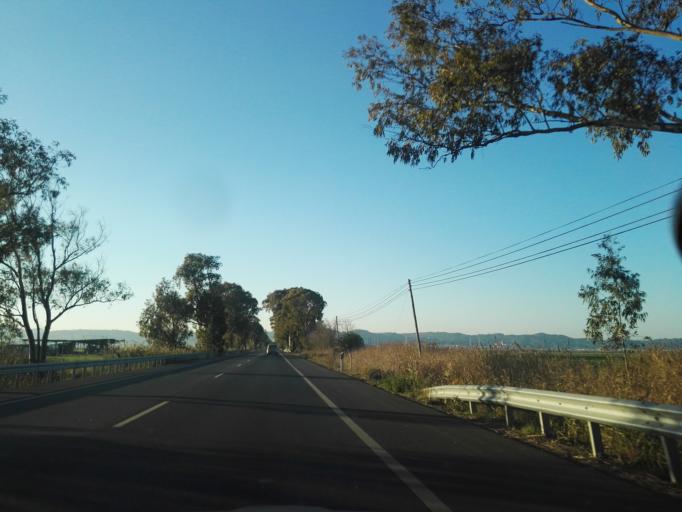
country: PT
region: Lisbon
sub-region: Vila Franca de Xira
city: Vila Franca de Xira
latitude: 38.9392
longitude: -8.9360
